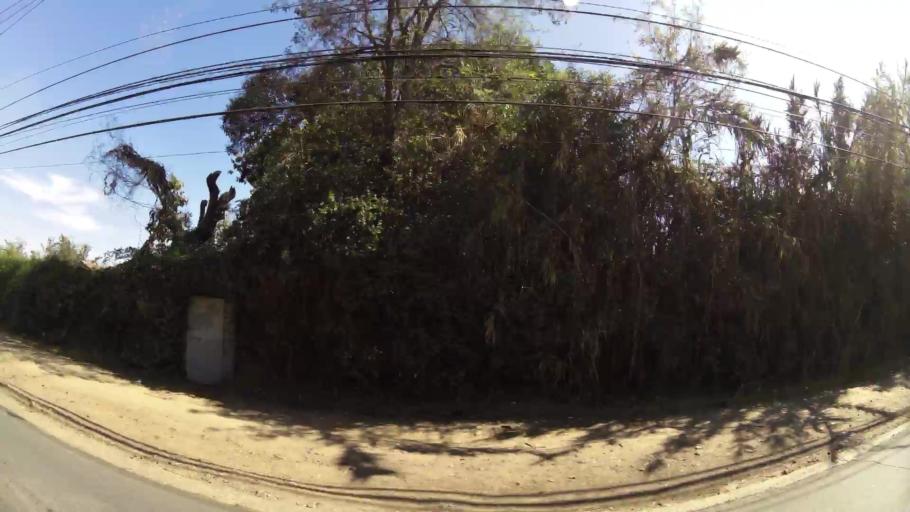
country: CL
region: Santiago Metropolitan
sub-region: Provincia de Santiago
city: Villa Presidente Frei, Nunoa, Santiago, Chile
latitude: -33.4536
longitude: -70.5206
